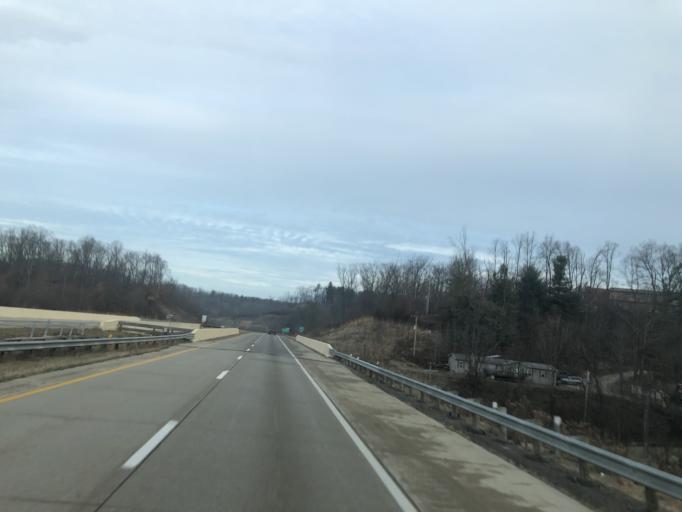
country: US
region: Ohio
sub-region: Athens County
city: Nelsonville
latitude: 39.4679
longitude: -82.2260
